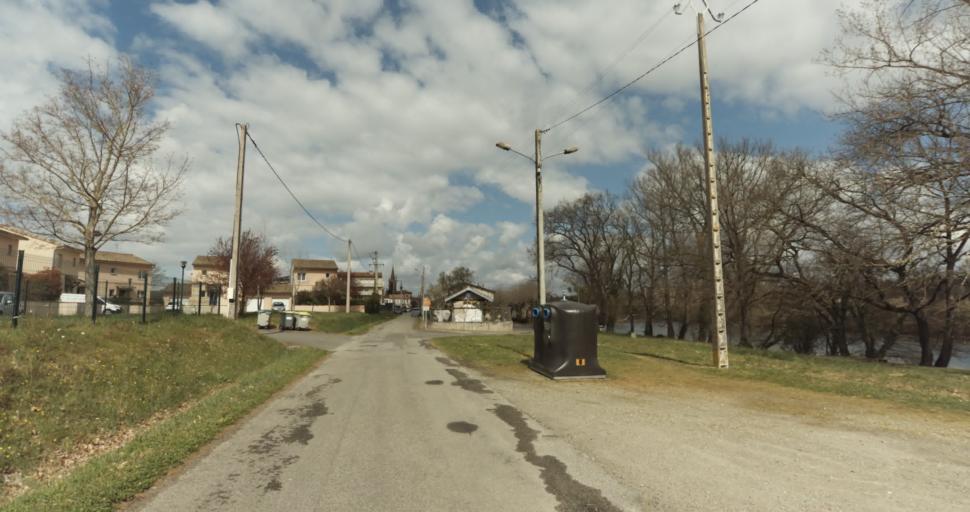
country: FR
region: Midi-Pyrenees
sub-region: Departement de la Haute-Garonne
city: Auterive
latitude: 43.3466
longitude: 1.4747
